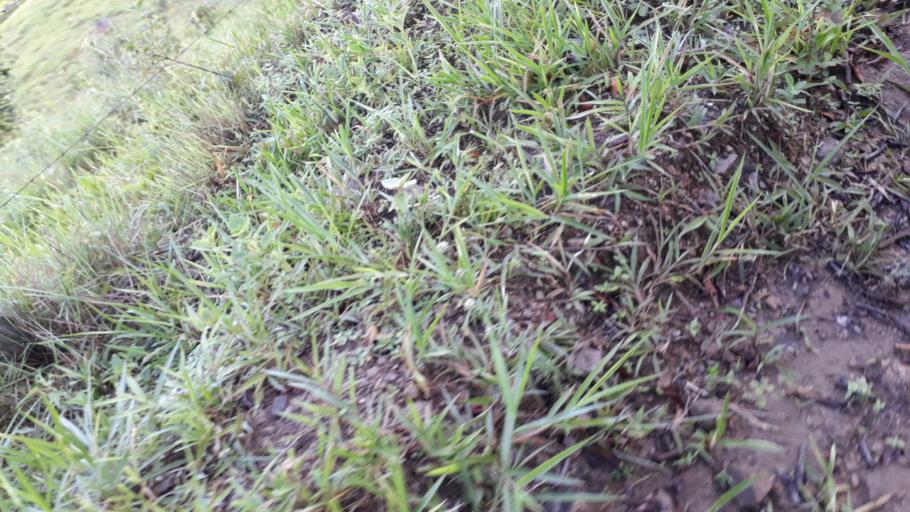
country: CO
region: Casanare
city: Nunchia
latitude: 5.6400
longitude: -72.4253
